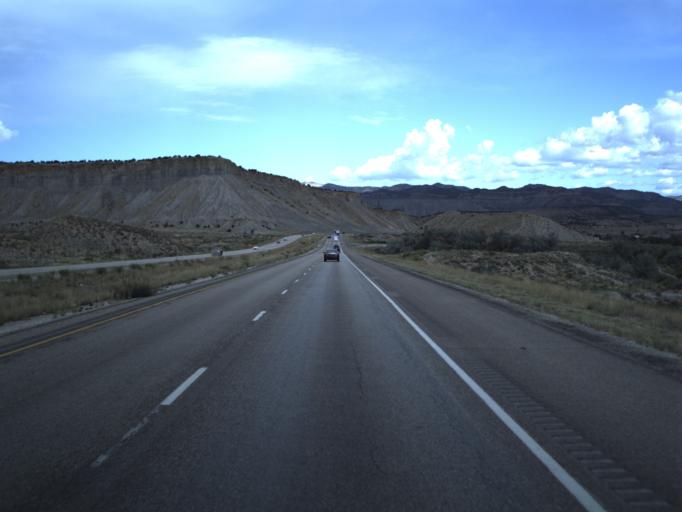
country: US
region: Utah
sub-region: Carbon County
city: Carbonville
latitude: 39.6208
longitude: -110.8559
